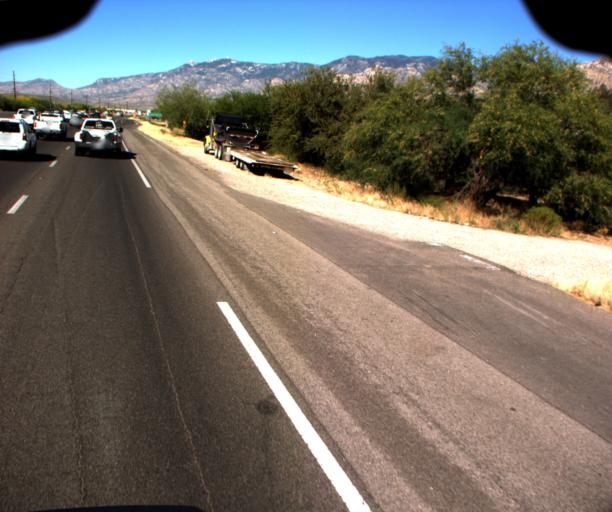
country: US
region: Arizona
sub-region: Pima County
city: Oro Valley
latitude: 32.4030
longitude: -110.9515
